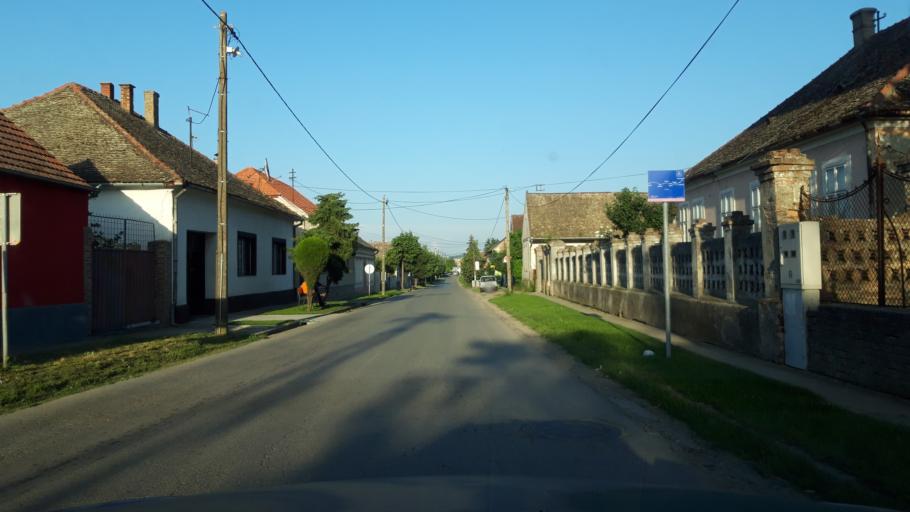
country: RS
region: Autonomna Pokrajina Vojvodina
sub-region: Juznobacki Okrug
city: Beocin
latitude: 45.2189
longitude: 19.6653
